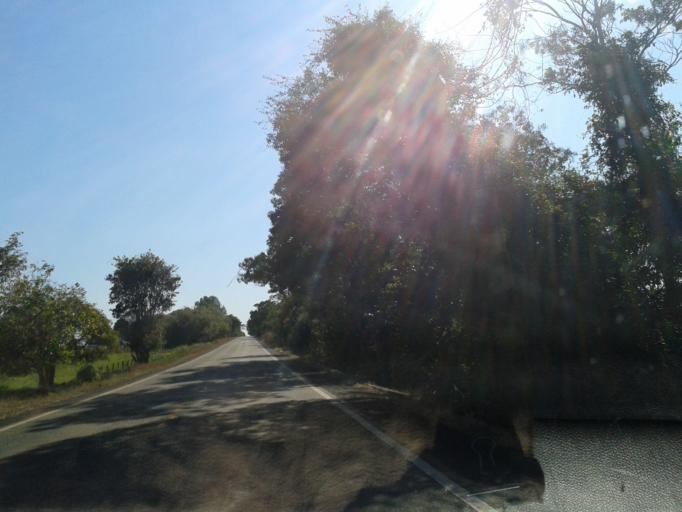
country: BR
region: Goias
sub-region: Mozarlandia
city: Mozarlandia
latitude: -14.6073
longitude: -50.5139
